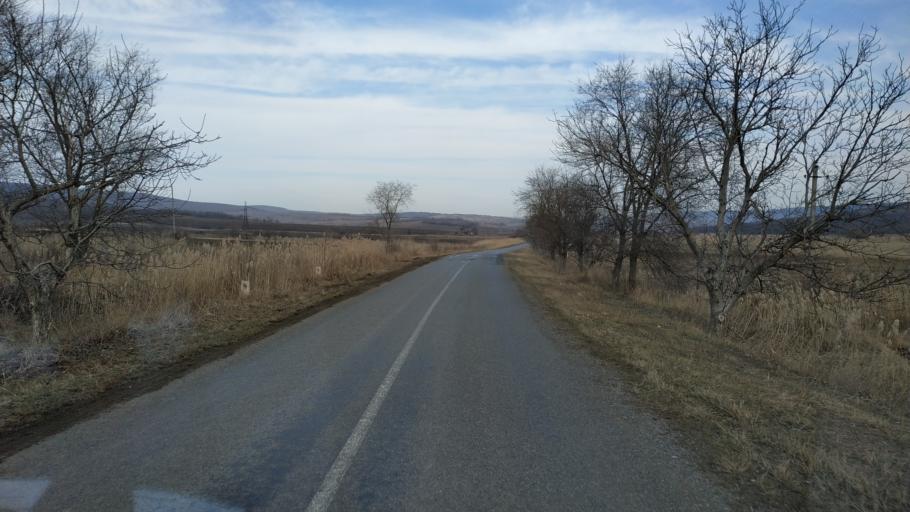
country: MD
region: Nisporeni
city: Nisporeni
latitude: 47.1030
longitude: 28.1270
